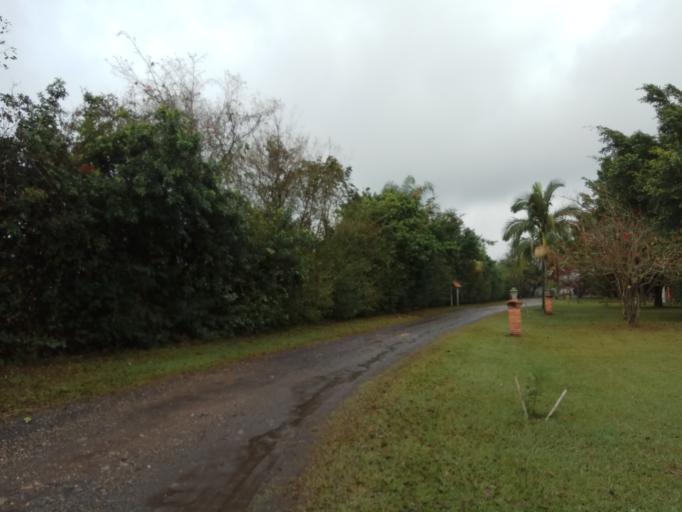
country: BR
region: Sao Paulo
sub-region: Charqueada
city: Charqueada
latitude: -22.4131
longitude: -47.7079
